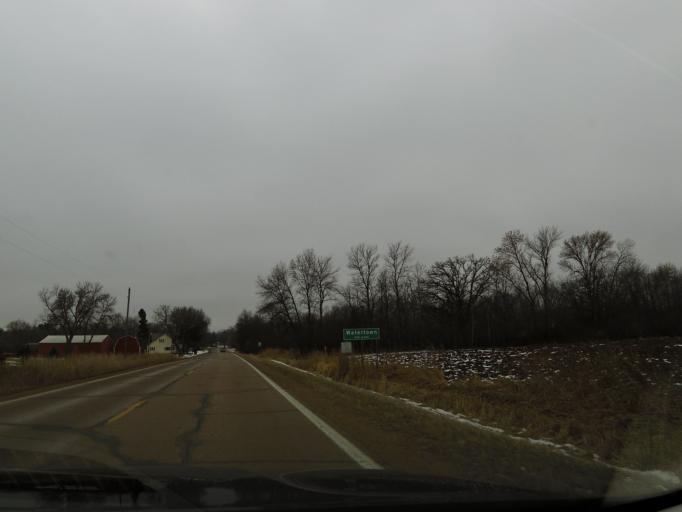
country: US
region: Minnesota
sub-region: Carver County
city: Watertown
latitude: 44.9748
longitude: -93.8495
